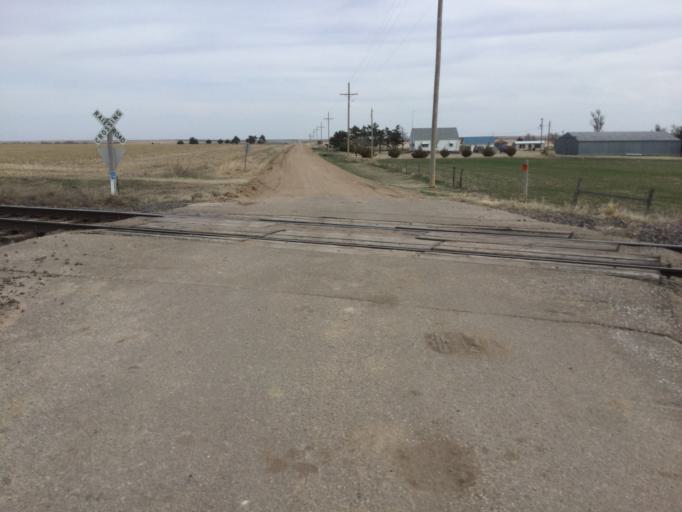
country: US
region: Kansas
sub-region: Trego County
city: WaKeeney
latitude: 38.9871
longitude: -99.7236
